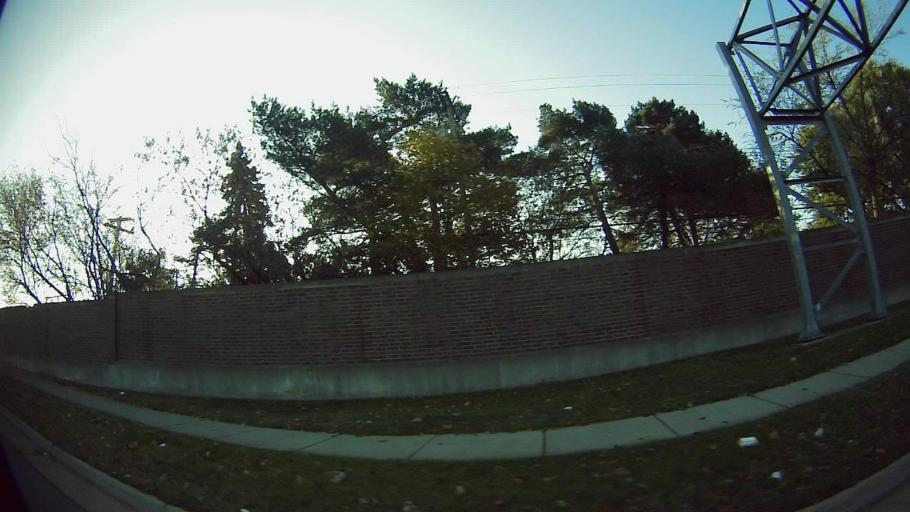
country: US
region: Michigan
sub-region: Oakland County
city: Pleasant Ridge
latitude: 42.4746
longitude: -83.1459
